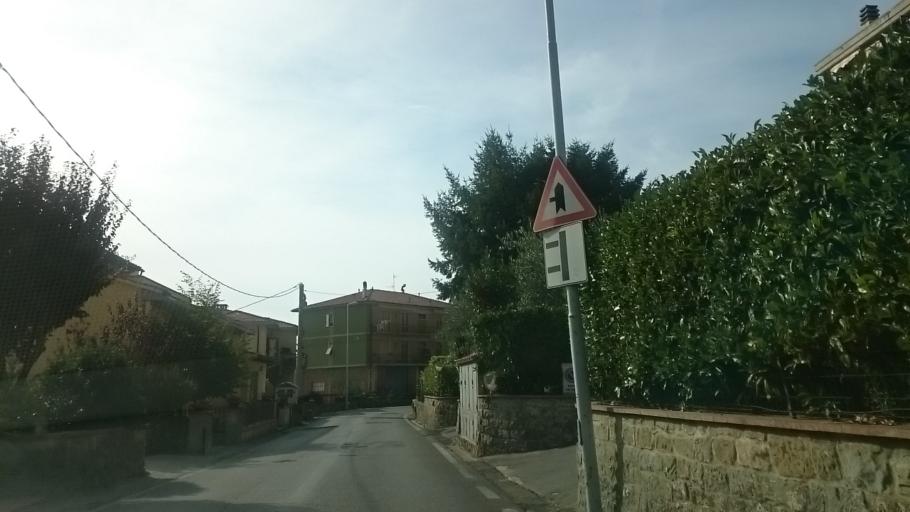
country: IT
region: Tuscany
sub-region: Province of Florence
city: Reggello
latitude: 43.6980
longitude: 11.5273
